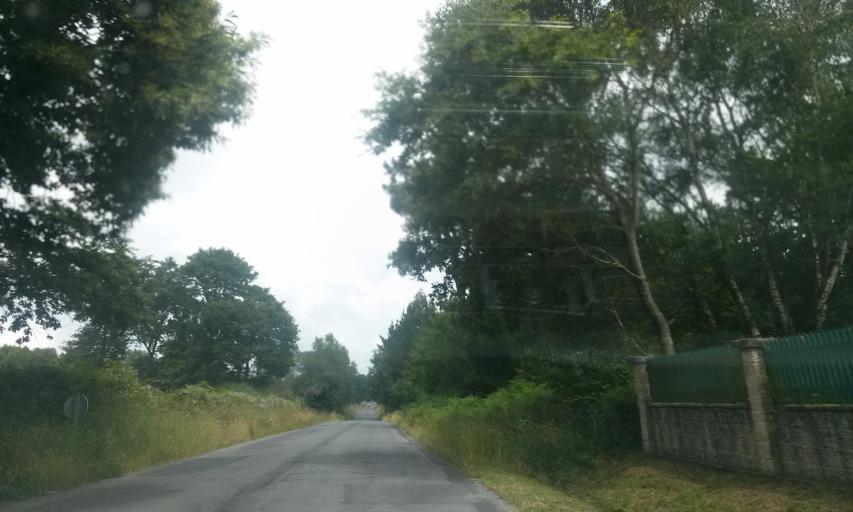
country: ES
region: Galicia
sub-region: Provincia de Lugo
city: Friol
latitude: 43.0940
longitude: -7.8090
